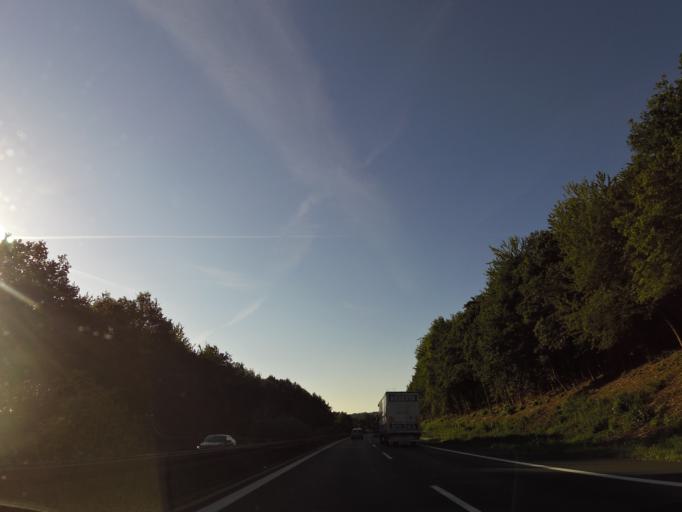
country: DE
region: Bavaria
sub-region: Upper Franconia
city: Schlusselfeld
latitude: 49.7392
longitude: 10.6538
